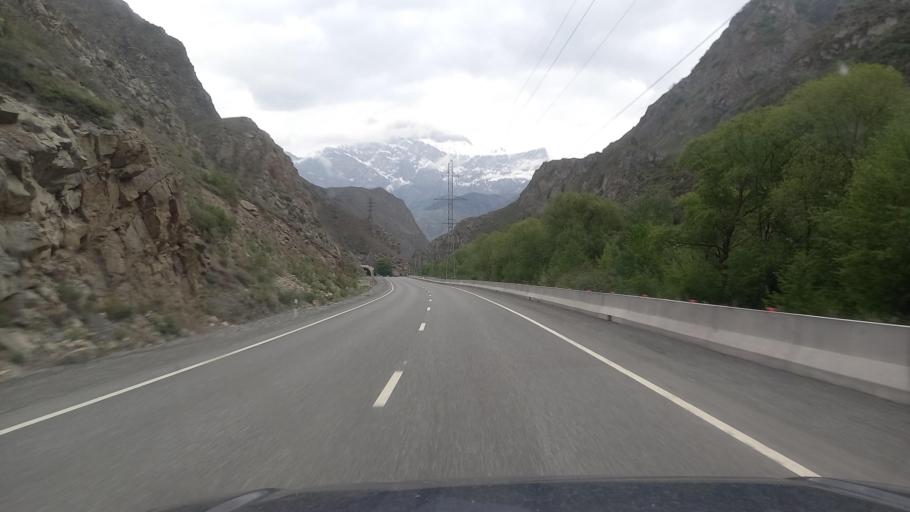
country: RU
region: North Ossetia
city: Mizur
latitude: 42.8555
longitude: 44.0975
